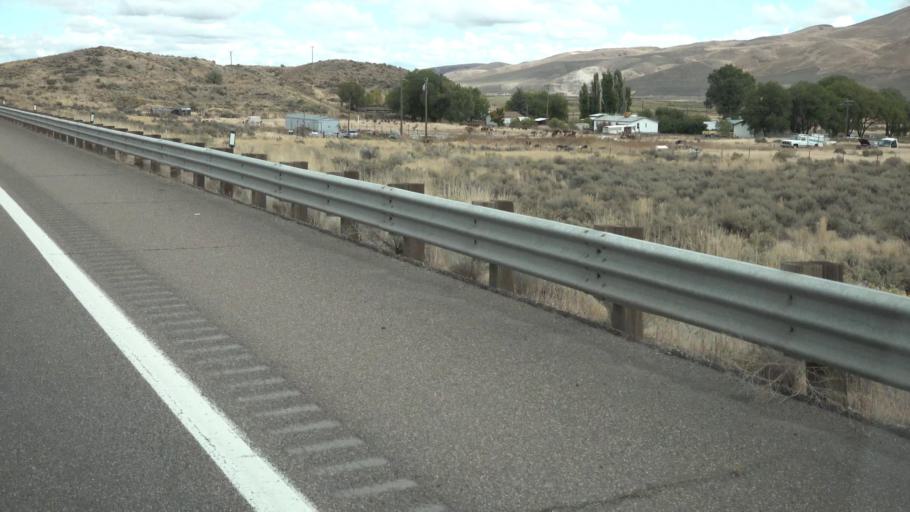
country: US
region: Nevada
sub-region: Elko County
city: Elko
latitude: 40.9050
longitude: -115.7004
